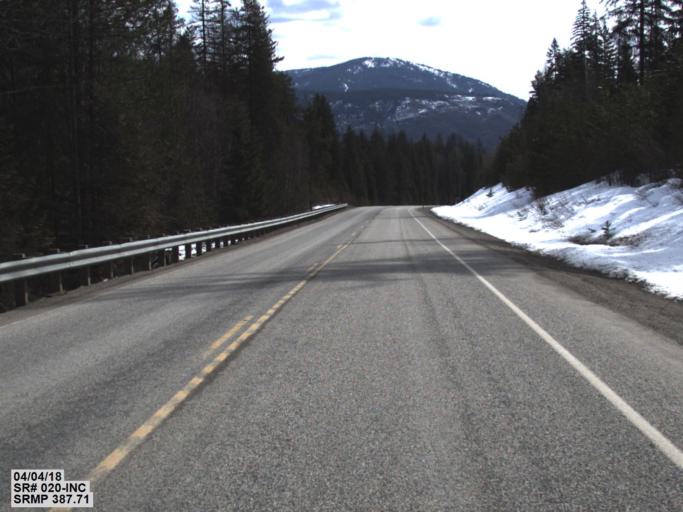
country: CA
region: British Columbia
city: Fruitvale
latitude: 48.6811
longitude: -117.4419
